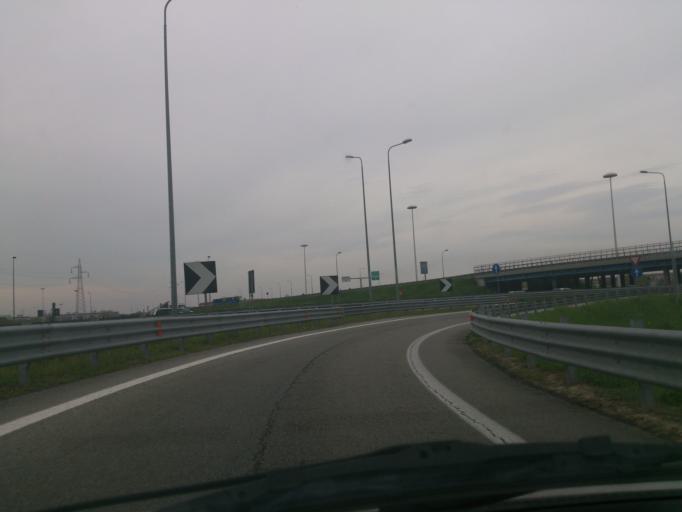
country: IT
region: Lombardy
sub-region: Citta metropolitana di Milano
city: San Donato Milanese
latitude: 45.4339
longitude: 9.2557
